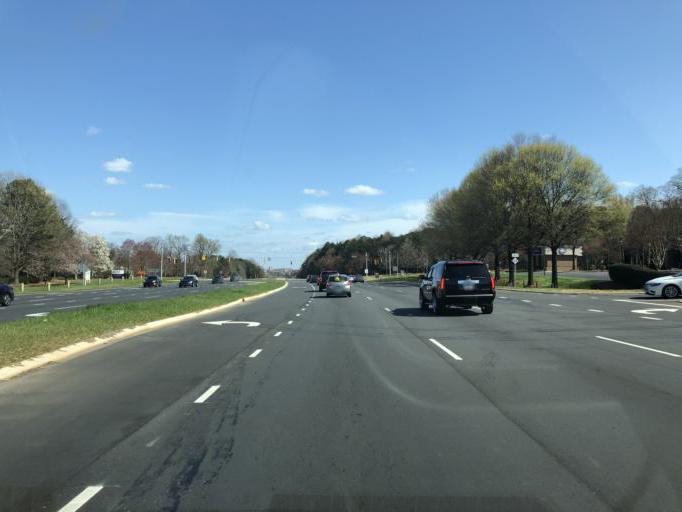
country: US
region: North Carolina
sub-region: Mecklenburg County
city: Charlotte
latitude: 35.3181
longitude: -80.7781
